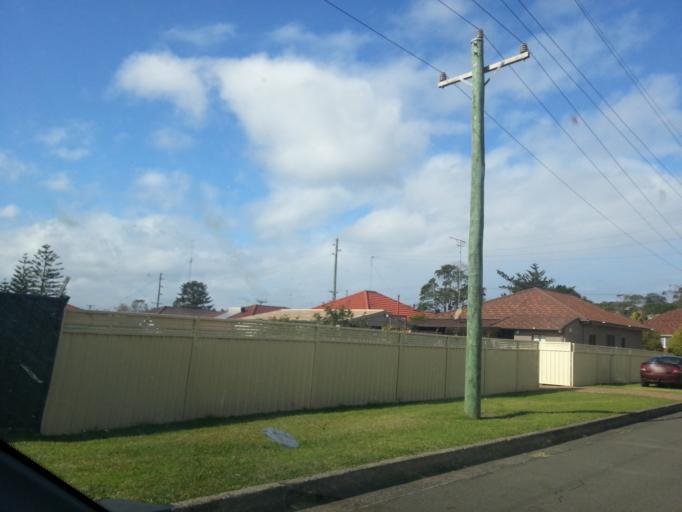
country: AU
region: New South Wales
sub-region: Wollongong
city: Port Kembla
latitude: -34.4809
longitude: 150.8983
